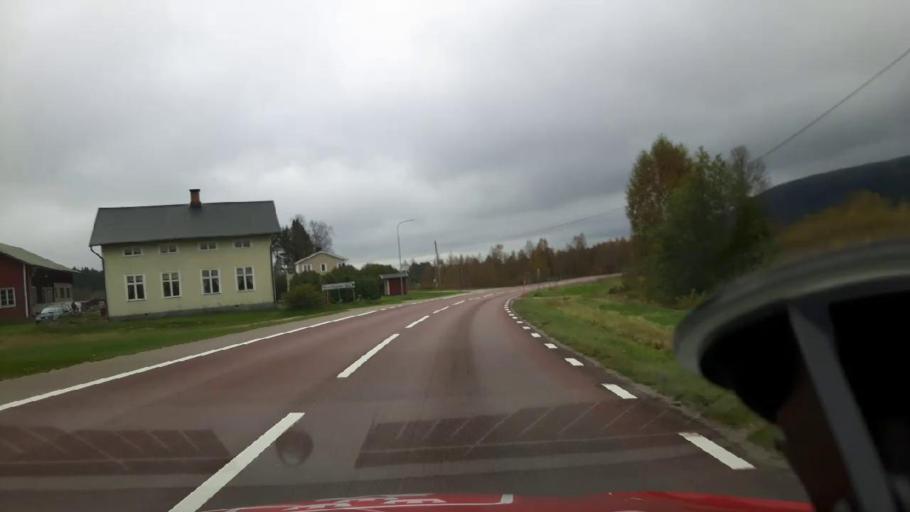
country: SE
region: Jaemtland
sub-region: Harjedalens Kommun
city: Sveg
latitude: 62.2791
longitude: 14.8061
